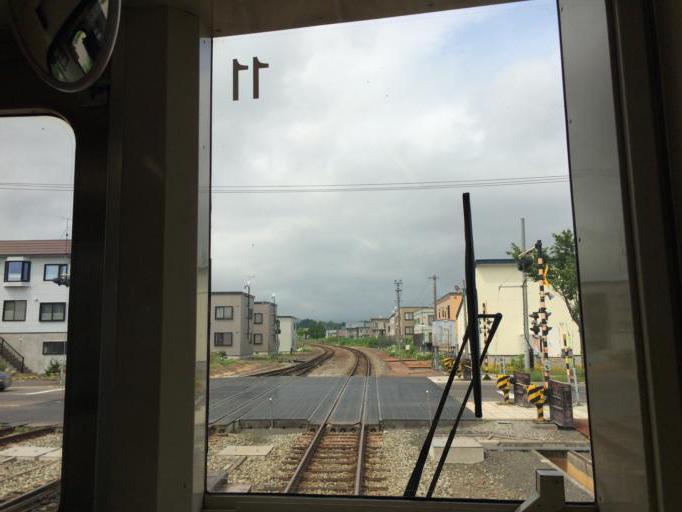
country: JP
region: Hokkaido
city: Niseko Town
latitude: 42.9042
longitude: 140.7457
